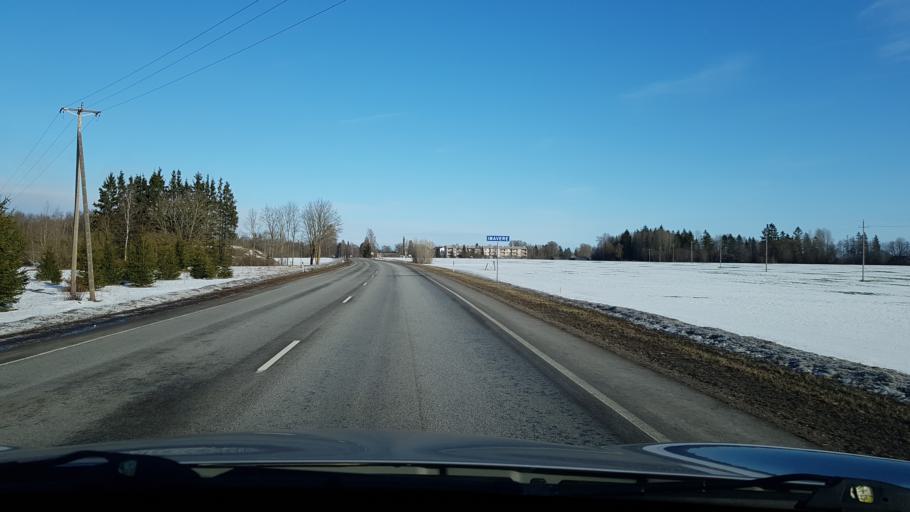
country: EE
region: Jogevamaa
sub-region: Poltsamaa linn
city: Poltsamaa
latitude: 58.7249
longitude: 25.7637
